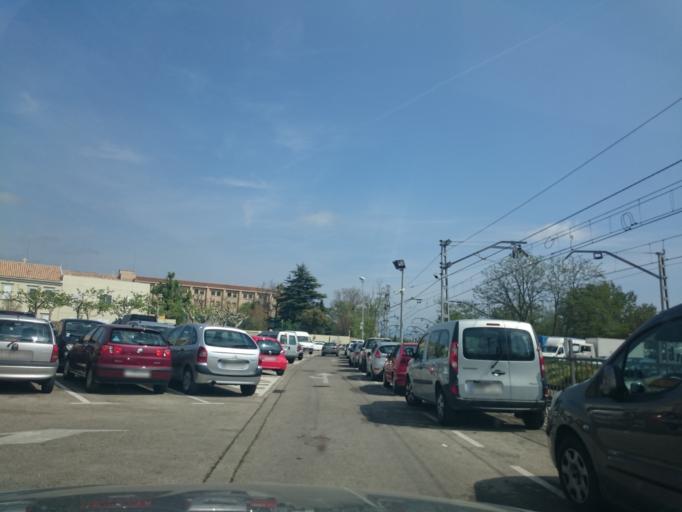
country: ES
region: Catalonia
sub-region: Provincia de Girona
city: Figueres
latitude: 42.2677
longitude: 2.9692
